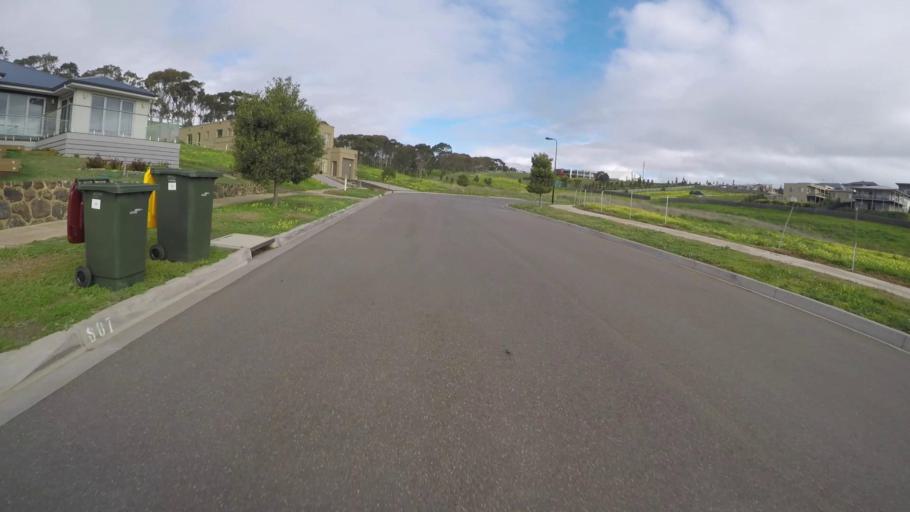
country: AU
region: Victoria
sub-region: Greater Geelong
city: Wandana Heights
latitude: -38.1575
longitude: 144.3081
